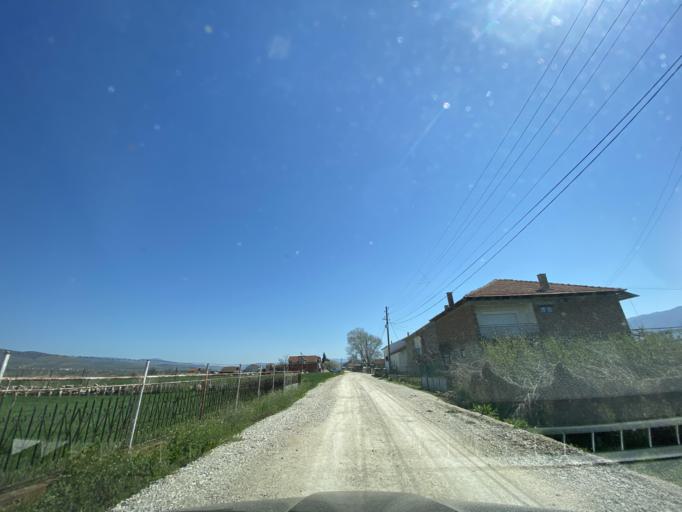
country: MK
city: Obleshevo
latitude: 41.8871
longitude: 22.3361
